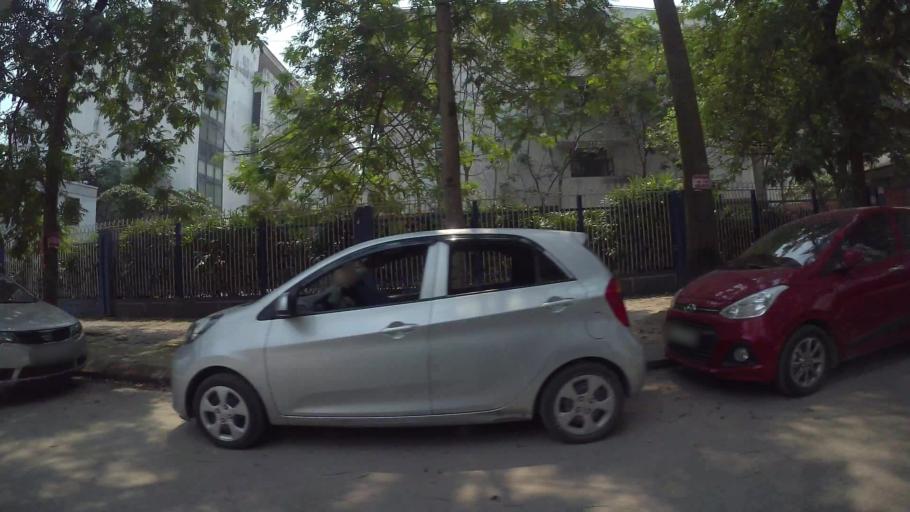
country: VN
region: Ha Noi
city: Thanh Xuan
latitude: 21.0077
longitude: 105.7995
